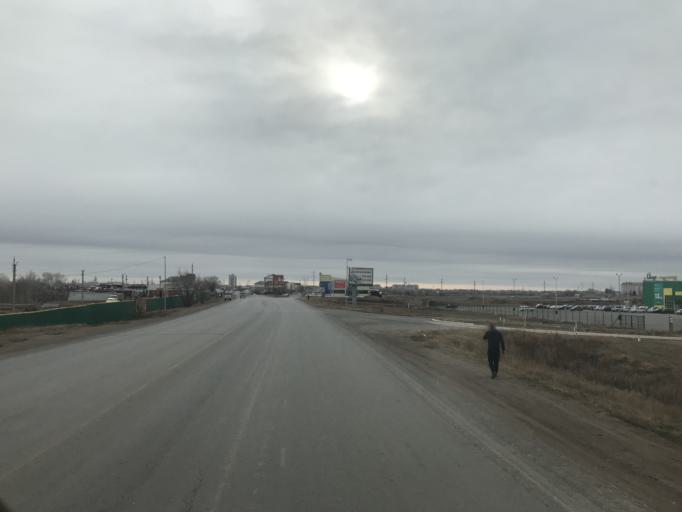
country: KZ
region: Batys Qazaqstan
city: Oral
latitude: 51.2668
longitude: 51.4061
